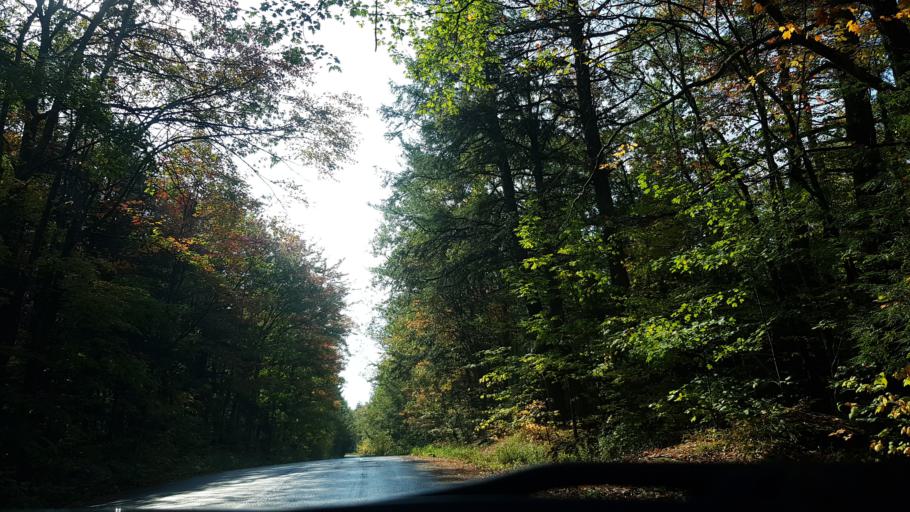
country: CA
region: Ontario
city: Bracebridge
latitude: 44.9825
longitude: -79.2628
